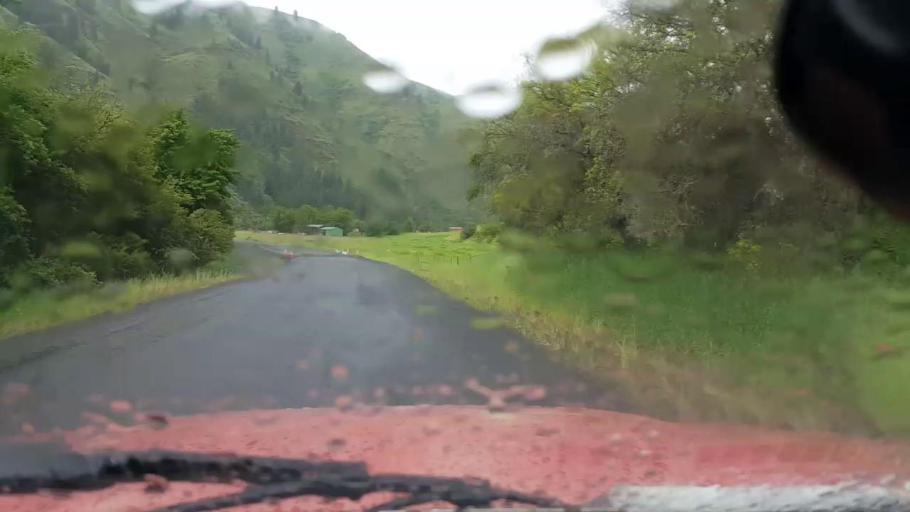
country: US
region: Washington
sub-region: Asotin County
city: Asotin
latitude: 46.0401
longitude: -117.2657
